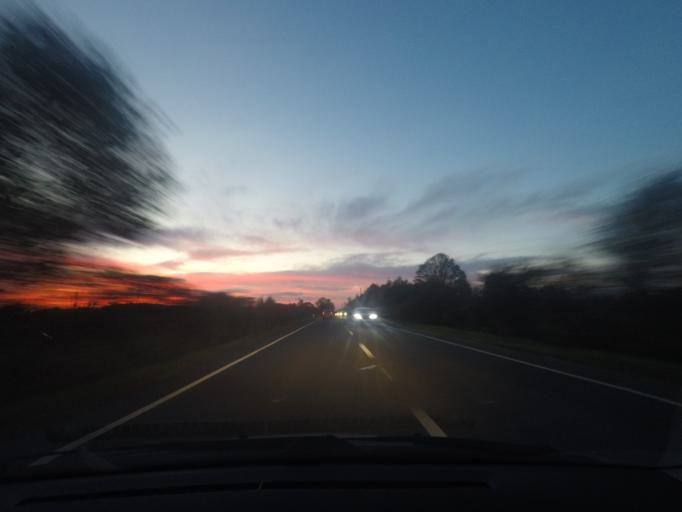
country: GB
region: England
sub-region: East Riding of Yorkshire
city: Thornton
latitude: 53.9349
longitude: -0.8467
